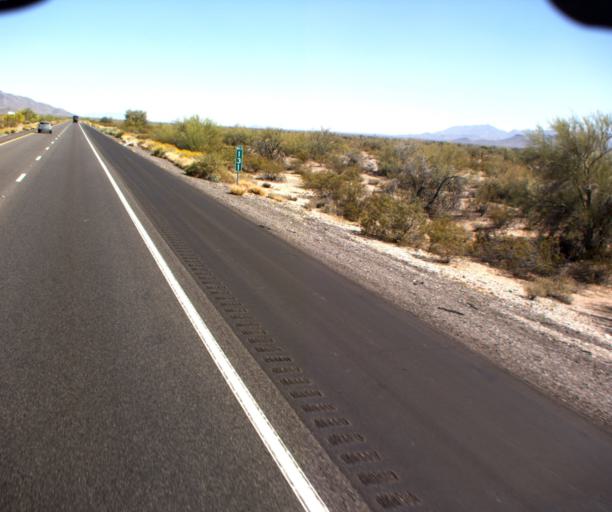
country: US
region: Arizona
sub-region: Maricopa County
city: Gila Bend
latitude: 32.8890
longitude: -112.4797
